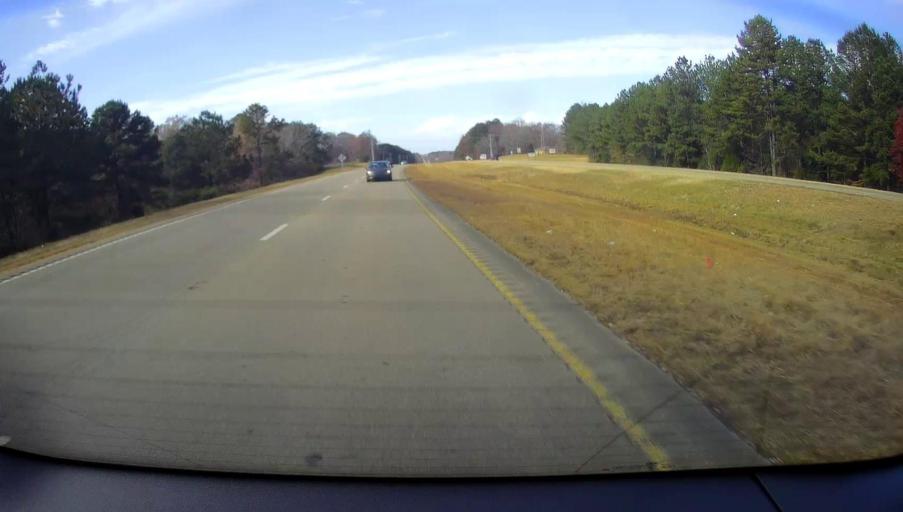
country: US
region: Mississippi
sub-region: Alcorn County
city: Farmington
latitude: 34.8822
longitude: -88.4488
